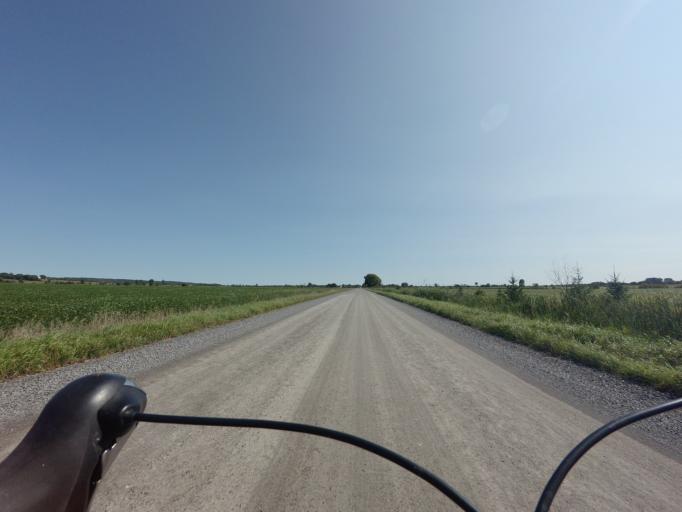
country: CA
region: Ontario
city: Arnprior
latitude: 45.3769
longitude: -76.1462
